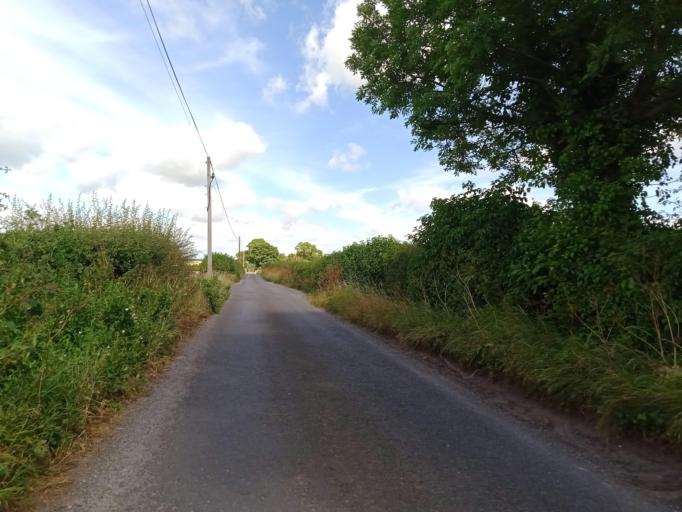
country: IE
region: Leinster
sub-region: Kilkenny
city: Kilkenny
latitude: 52.6361
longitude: -7.2181
